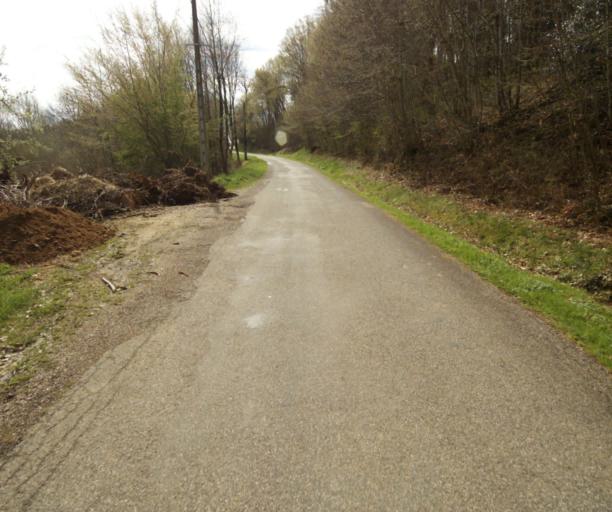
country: FR
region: Limousin
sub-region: Departement de la Correze
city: Laguenne
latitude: 45.2377
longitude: 1.8400
